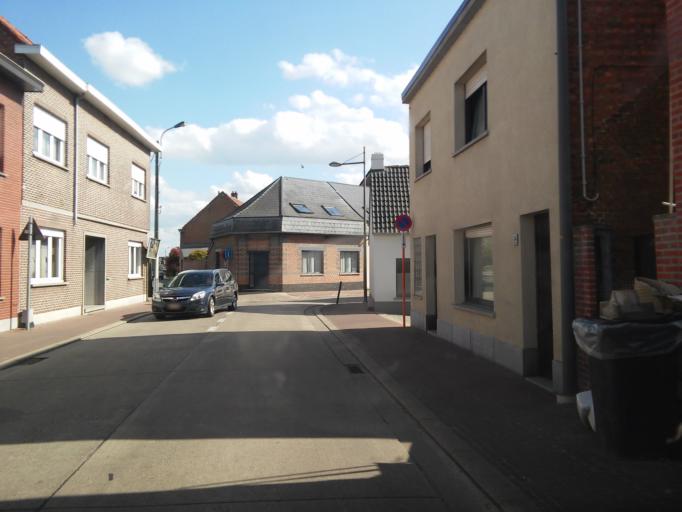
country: BE
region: Flanders
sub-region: Provincie Antwerpen
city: Puurs
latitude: 51.0894
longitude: 4.3113
